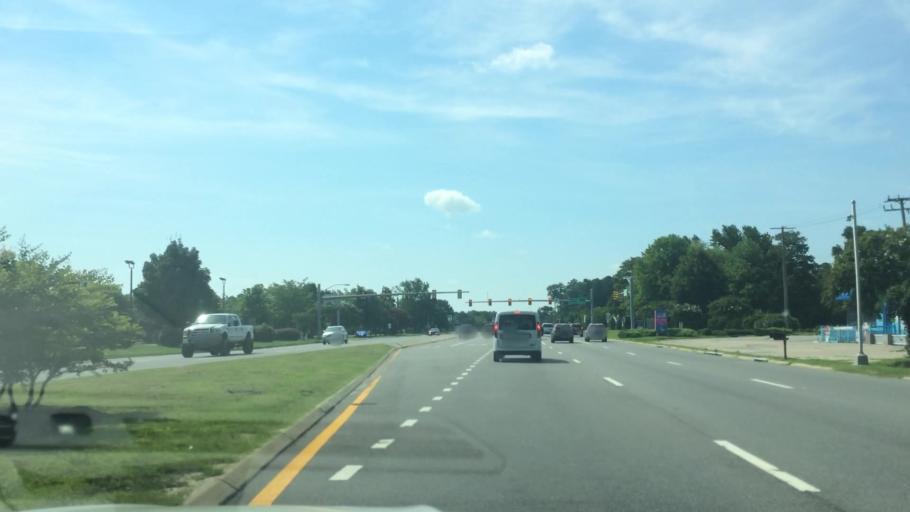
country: US
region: Virginia
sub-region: York County
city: Yorktown
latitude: 37.1618
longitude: -76.4642
